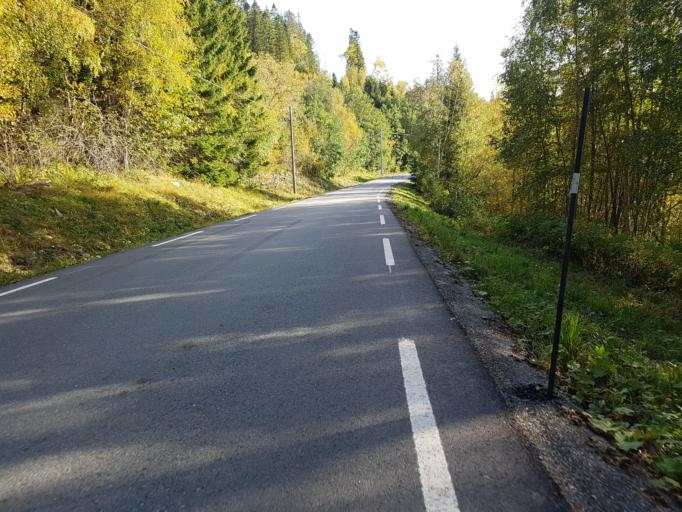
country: NO
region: Sor-Trondelag
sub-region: Malvik
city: Malvik
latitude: 63.3668
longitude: 10.6221
